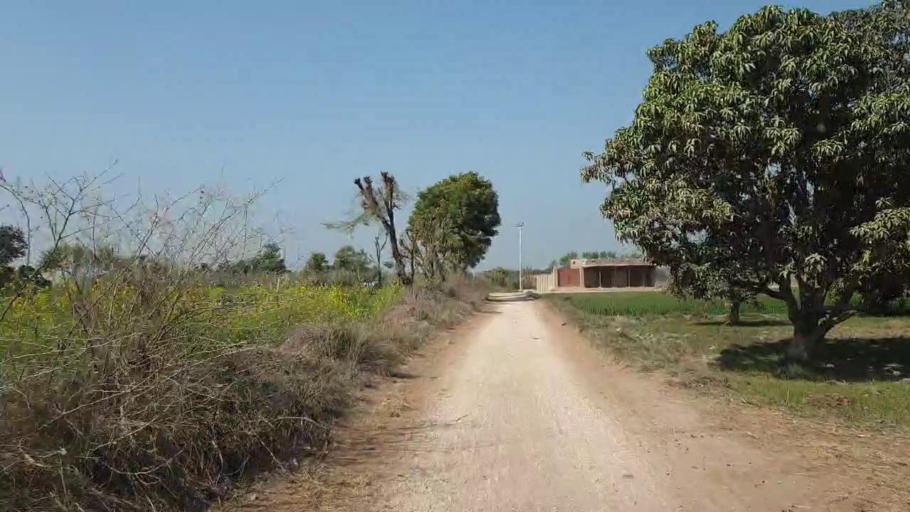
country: PK
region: Sindh
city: Hala
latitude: 25.9105
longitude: 68.4306
